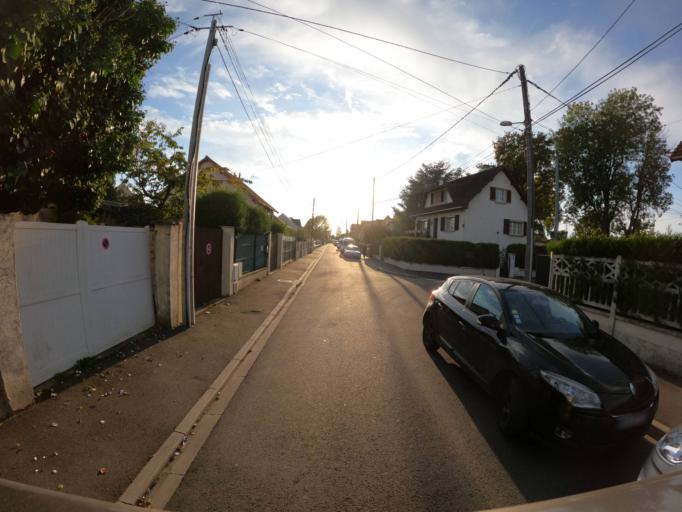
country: FR
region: Ile-de-France
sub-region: Departement de Seine-et-Marne
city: Emerainville
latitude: 48.8029
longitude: 2.6180
